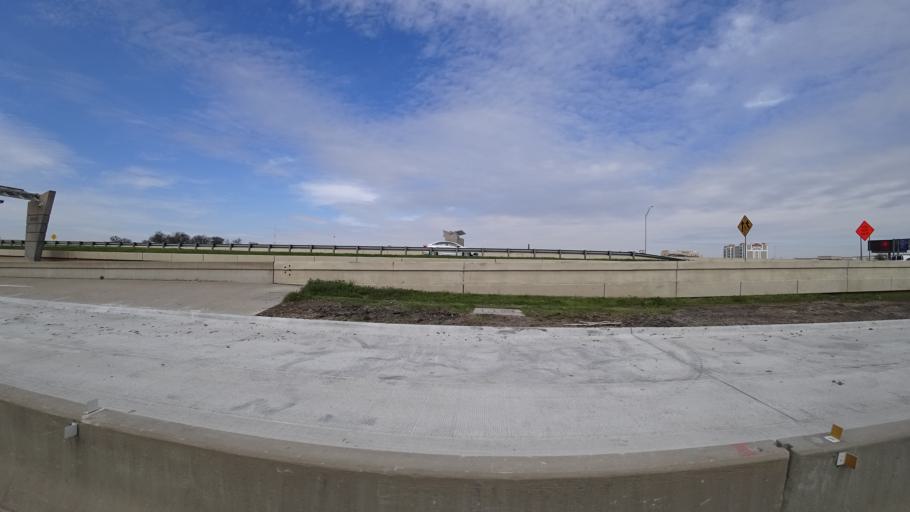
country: US
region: Texas
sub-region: Denton County
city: Lewisville
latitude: 32.9929
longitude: -96.9700
